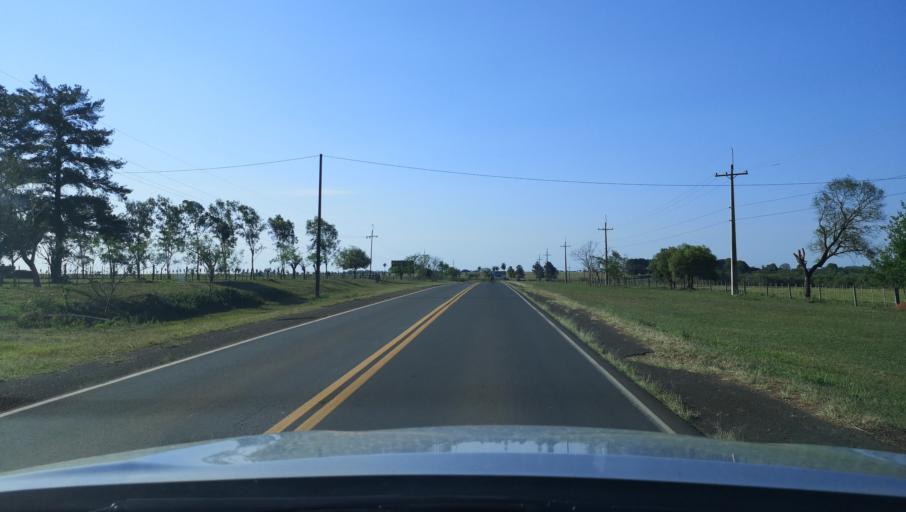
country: PY
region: Misiones
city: Santa Maria
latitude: -26.8483
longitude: -57.0370
